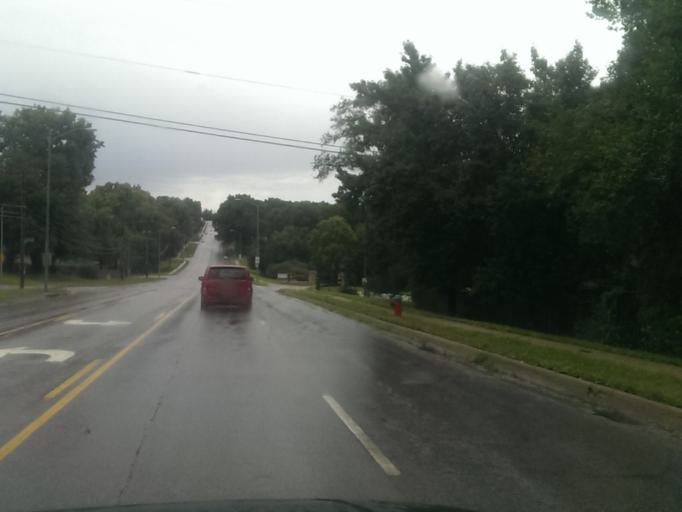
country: US
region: Kansas
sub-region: Johnson County
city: Leawood
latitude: 38.9272
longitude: -94.5832
